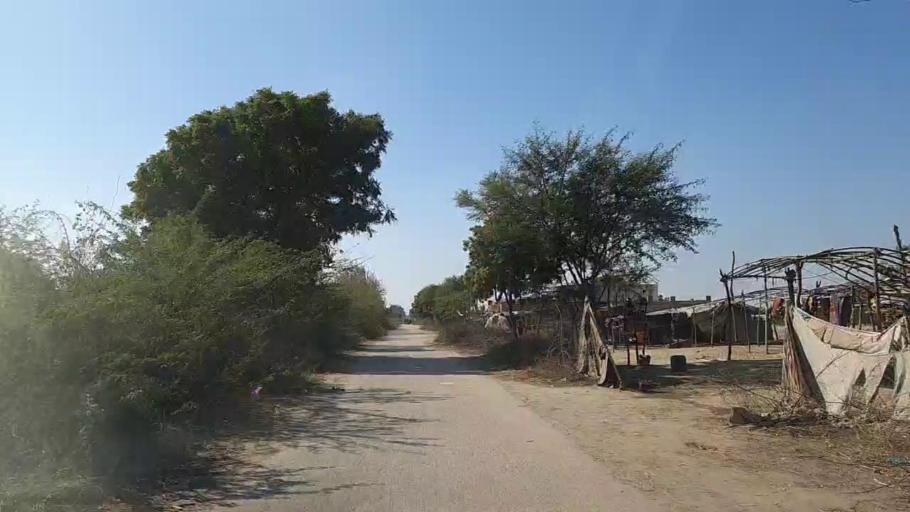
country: PK
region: Sindh
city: Nawabshah
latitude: 26.2447
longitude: 68.4381
